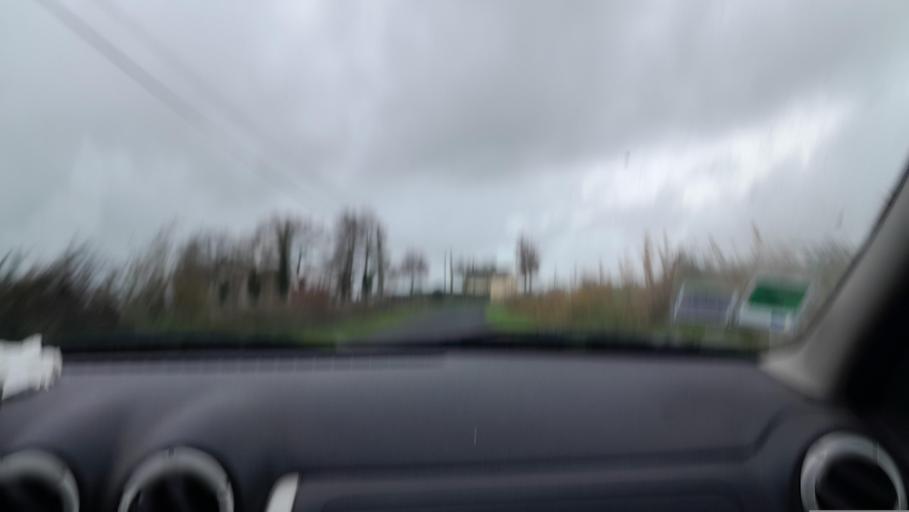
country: FR
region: Brittany
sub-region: Departement d'Ille-et-Vilaine
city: La Guerche-de-Bretagne
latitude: 47.9108
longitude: -1.1450
